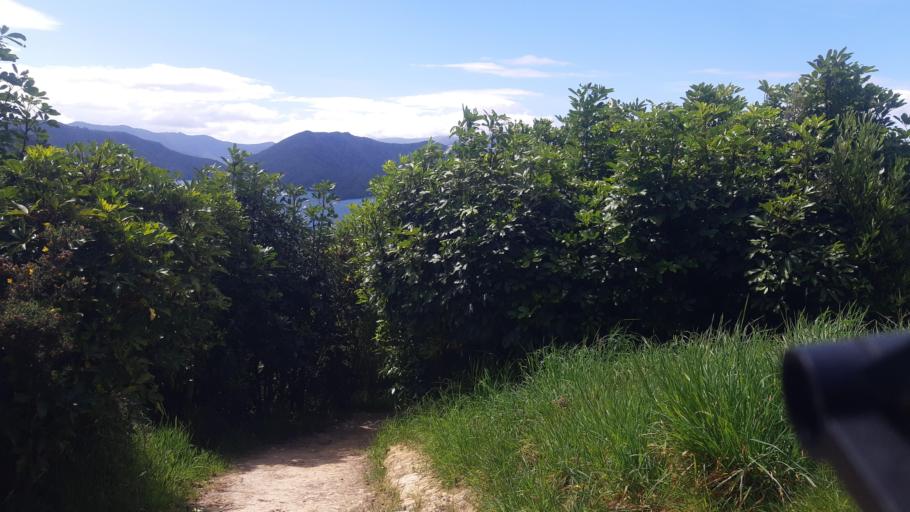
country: NZ
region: Marlborough
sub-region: Marlborough District
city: Picton
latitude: -41.2600
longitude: 174.0352
